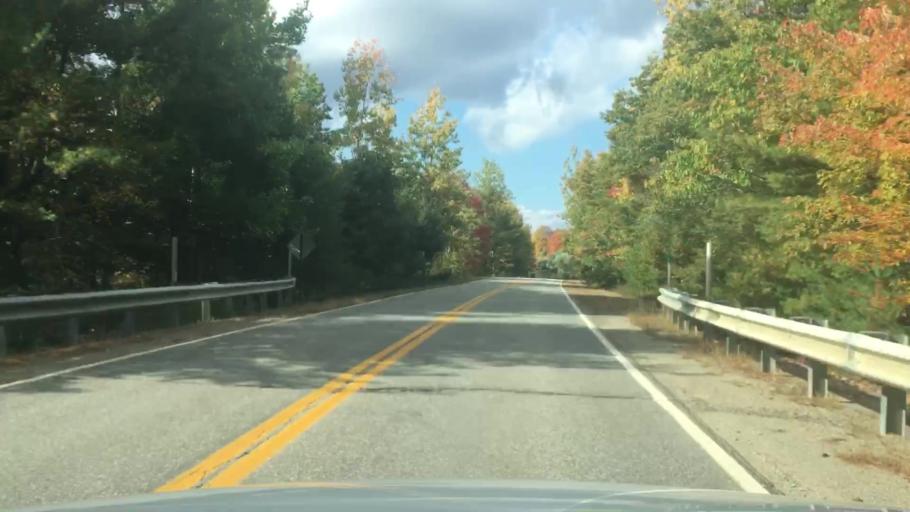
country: US
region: Maine
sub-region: Knox County
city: Washington
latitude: 44.3130
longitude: -69.3522
